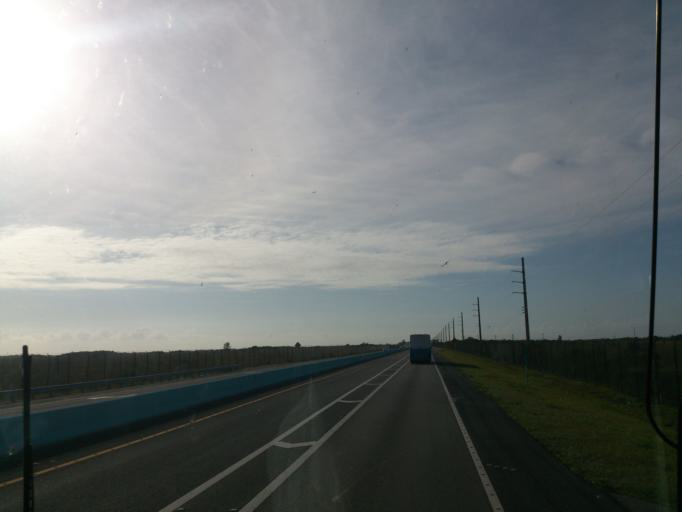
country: US
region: Florida
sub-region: Miami-Dade County
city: Florida City
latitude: 25.3815
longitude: -80.4647
